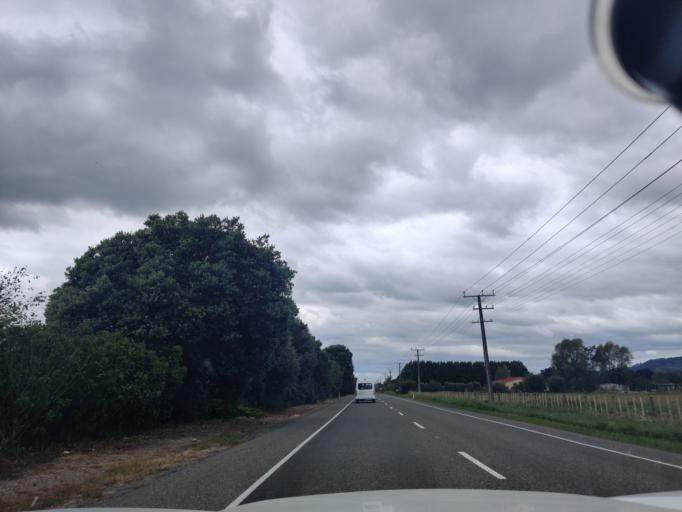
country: NZ
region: Manawatu-Wanganui
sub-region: Horowhenua District
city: Levin
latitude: -40.6371
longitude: 175.2995
